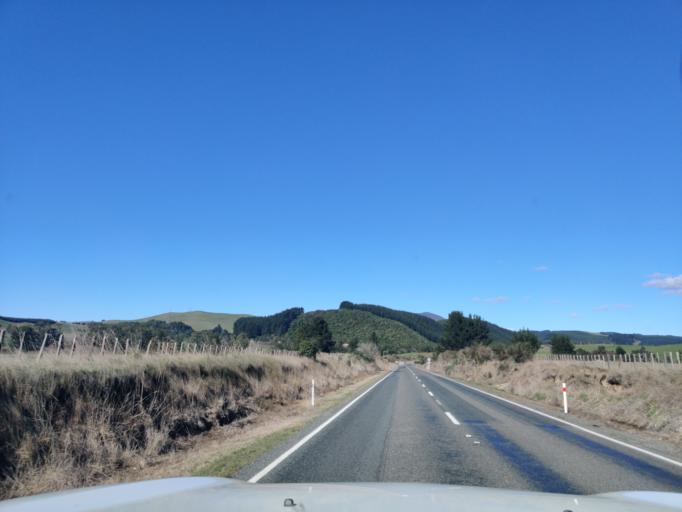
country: NZ
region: Waikato
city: Turangi
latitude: -38.8680
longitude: 175.6847
